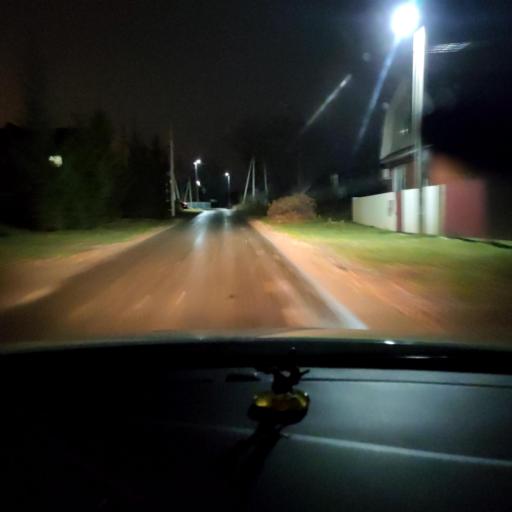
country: RU
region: Tatarstan
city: Vysokaya Gora
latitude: 55.7994
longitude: 49.4073
